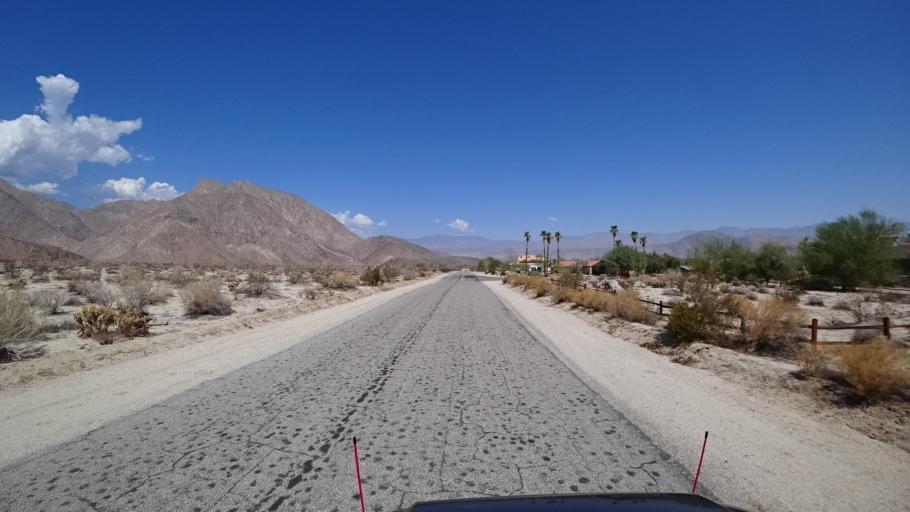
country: US
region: California
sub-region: San Diego County
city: Borrego Springs
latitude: 33.2600
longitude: -116.3995
